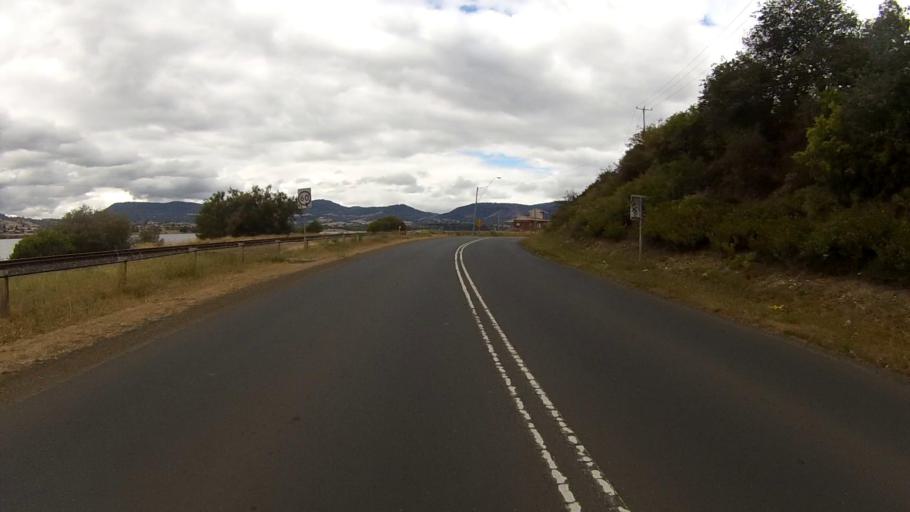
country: AU
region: Tasmania
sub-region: Glenorchy
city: Granton
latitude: -42.7517
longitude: 147.2312
